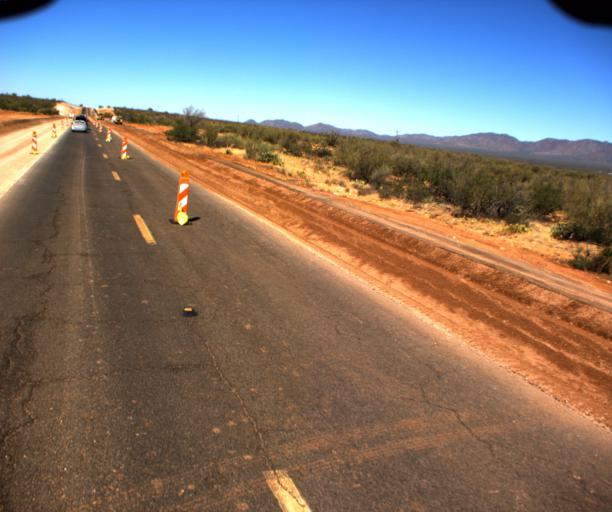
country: US
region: Arizona
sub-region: Pima County
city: Sells
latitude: 32.0039
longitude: -111.6825
